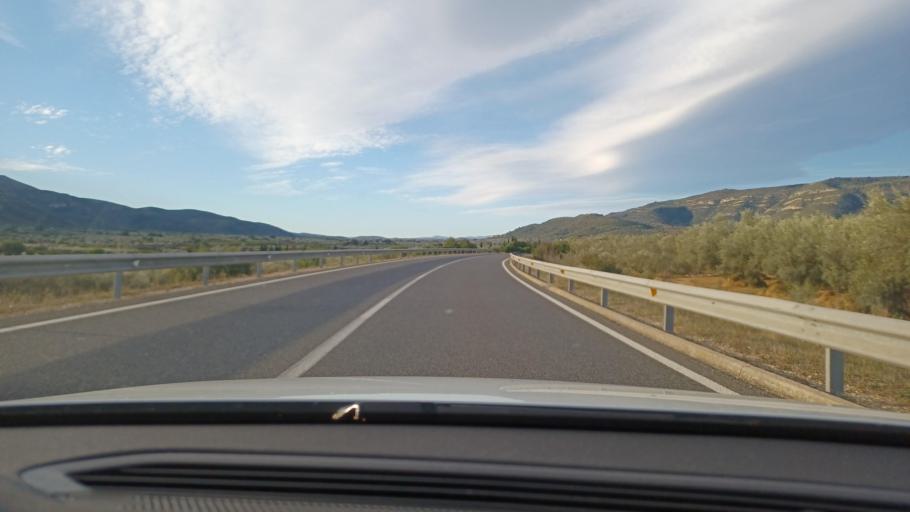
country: ES
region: Catalonia
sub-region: Provincia de Tarragona
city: Masdenverge
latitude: 40.6718
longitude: 0.5250
